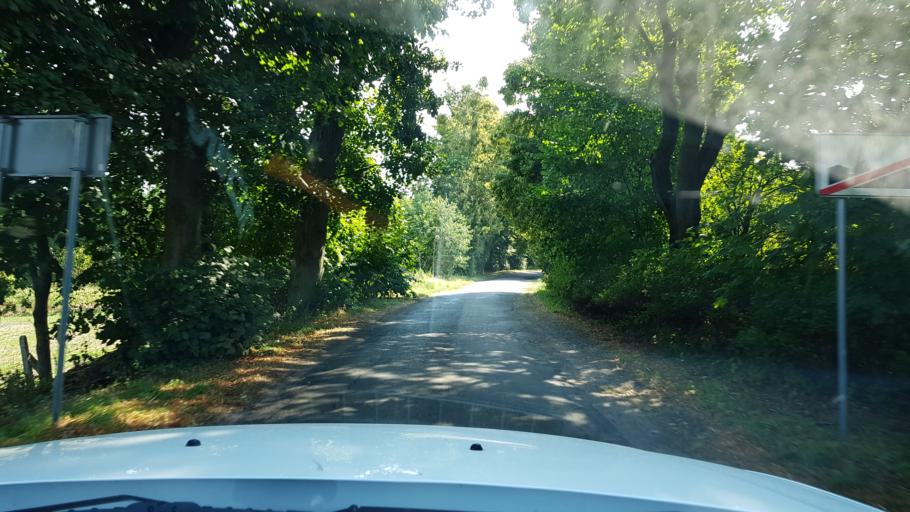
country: PL
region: West Pomeranian Voivodeship
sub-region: Powiat gryfinski
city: Chojna
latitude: 52.9515
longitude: 14.5067
